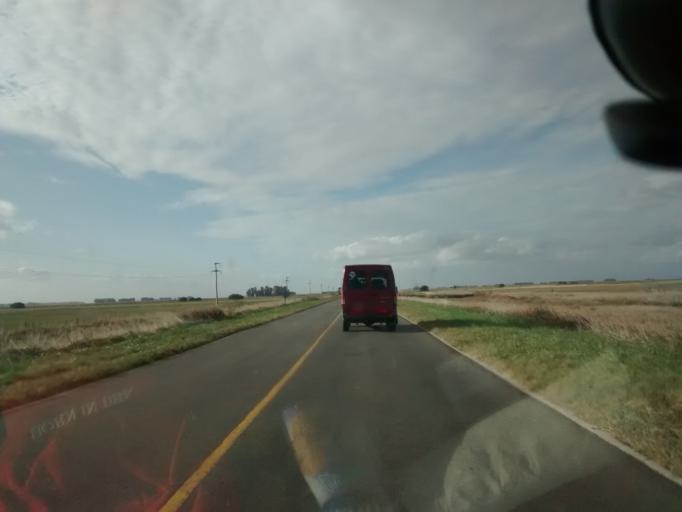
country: AR
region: Buenos Aires
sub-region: Partido de Ayacucho
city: Ayacucho
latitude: -36.8175
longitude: -58.5666
